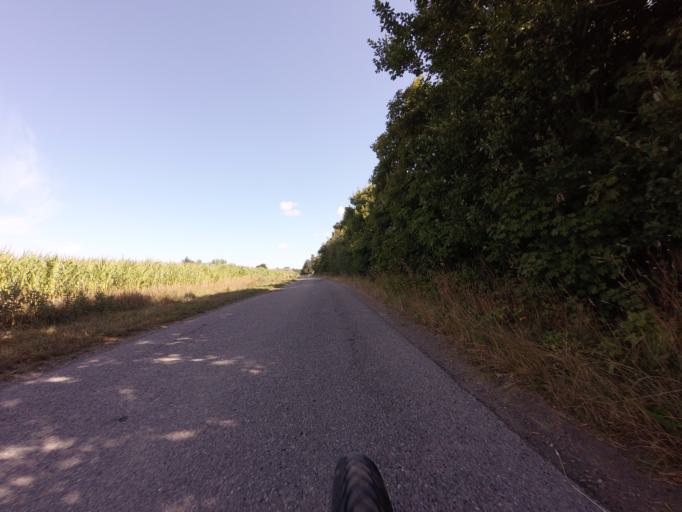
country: DK
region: North Denmark
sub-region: Hjorring Kommune
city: Vra
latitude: 57.4055
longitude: 9.9559
